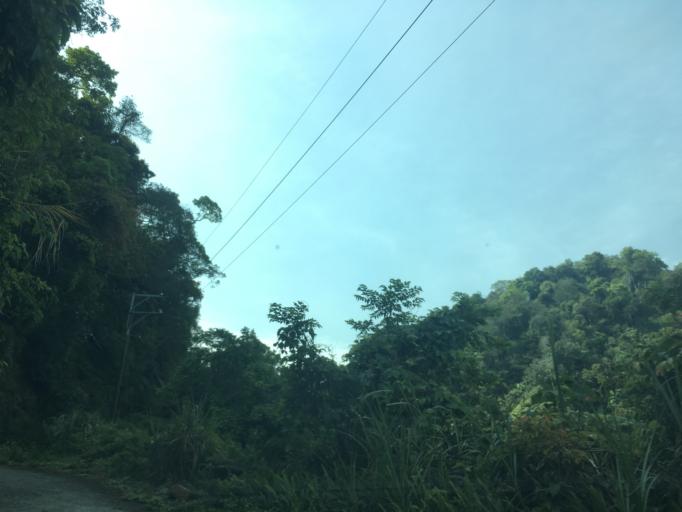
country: TW
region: Taiwan
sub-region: Taichung City
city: Taichung
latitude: 24.1408
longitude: 120.8205
